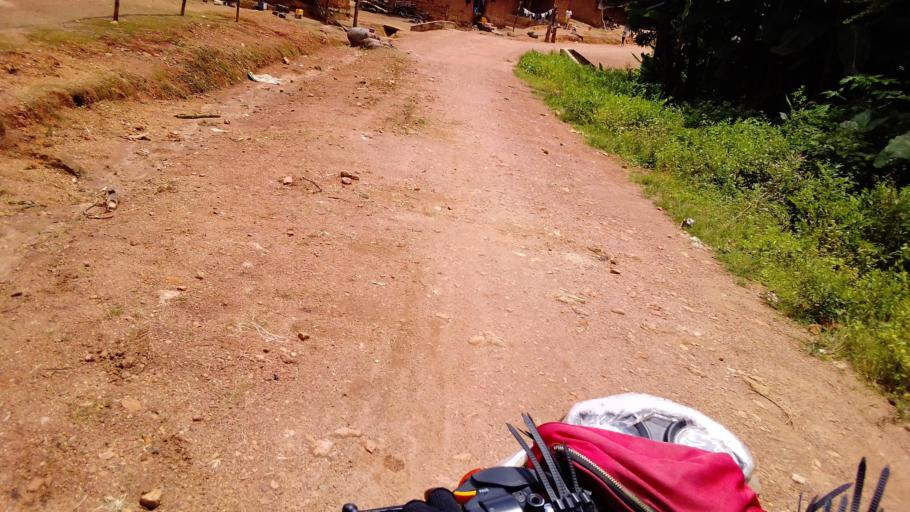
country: SL
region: Eastern Province
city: Koidu
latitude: 8.6736
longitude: -10.9374
